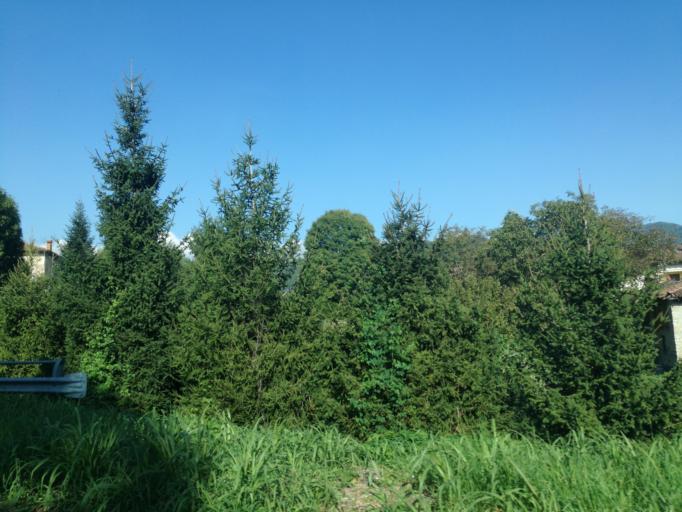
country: IT
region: Lombardy
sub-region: Provincia di Lecco
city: Imbersago
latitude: 45.7106
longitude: 9.4484
